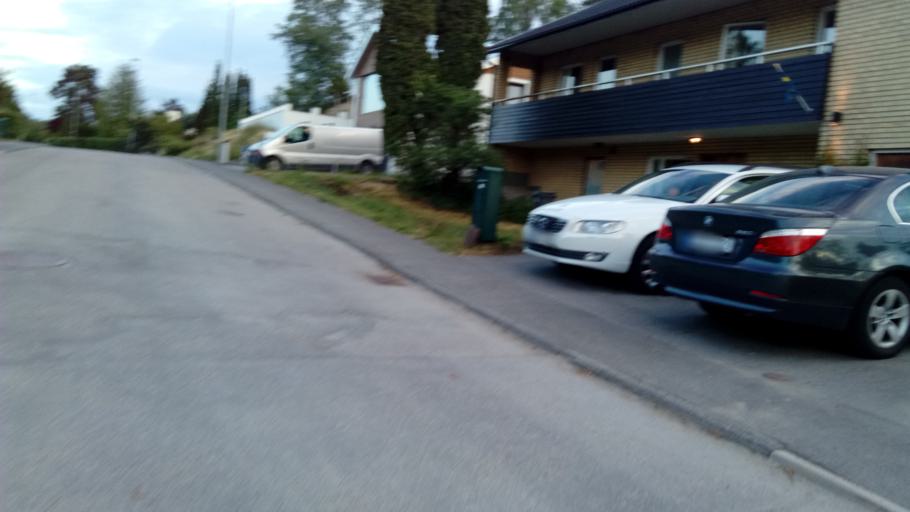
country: SE
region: Stockholm
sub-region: Tyreso Kommun
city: Bollmora
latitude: 59.2431
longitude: 18.2480
